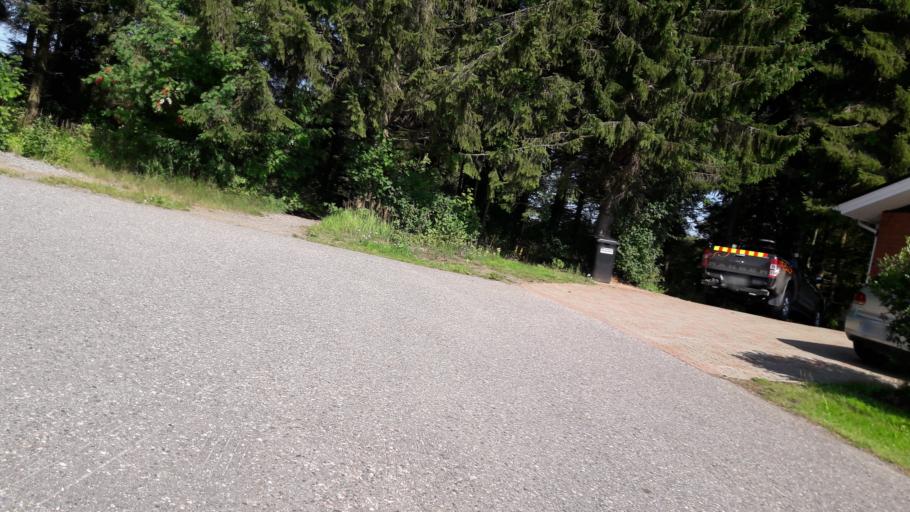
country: FI
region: North Karelia
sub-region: Joensuu
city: Joensuu
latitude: 62.5345
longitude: 29.8353
